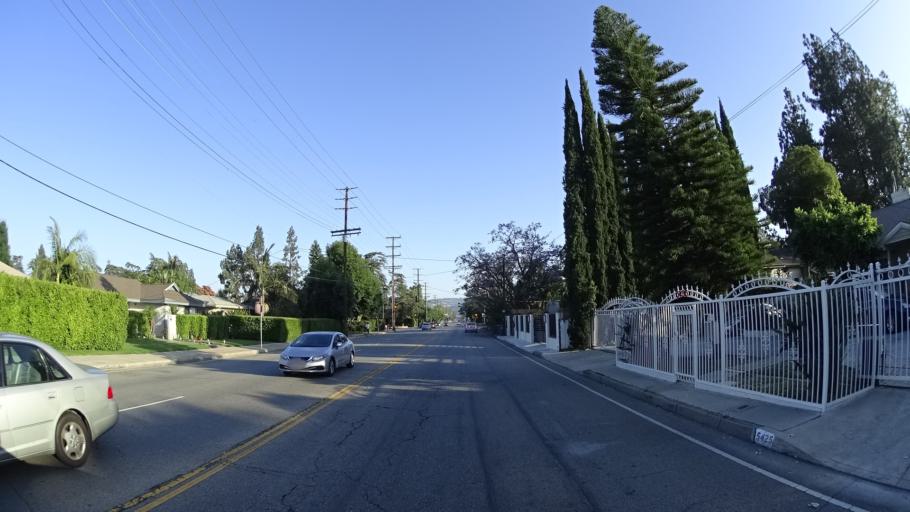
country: US
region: California
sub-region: Los Angeles County
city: Van Nuys
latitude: 34.1695
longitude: -118.4400
